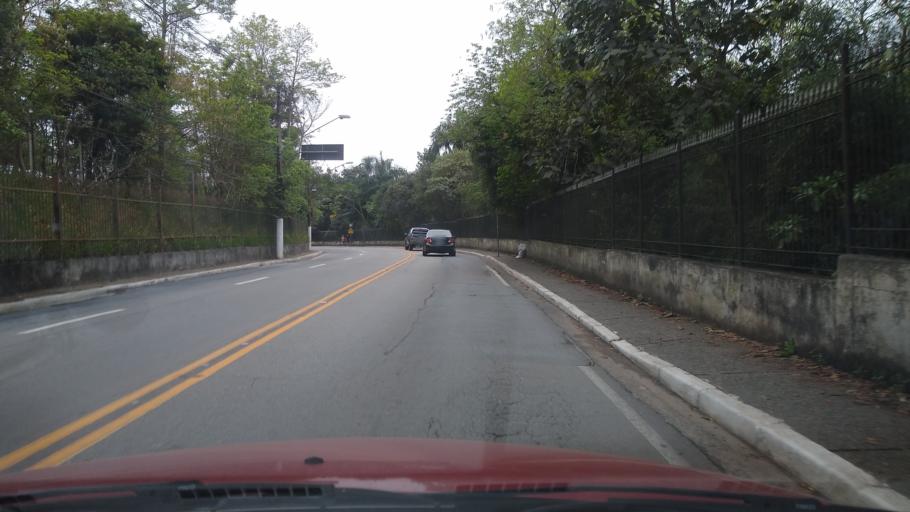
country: BR
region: Sao Paulo
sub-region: Diadema
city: Diadema
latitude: -23.6526
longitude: -46.6186
